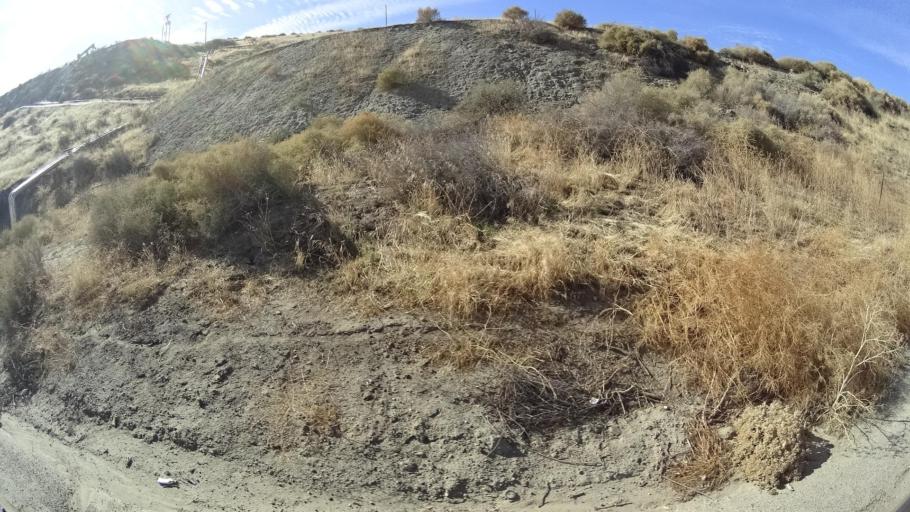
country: US
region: California
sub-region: Kern County
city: Oildale
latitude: 35.5742
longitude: -118.9600
